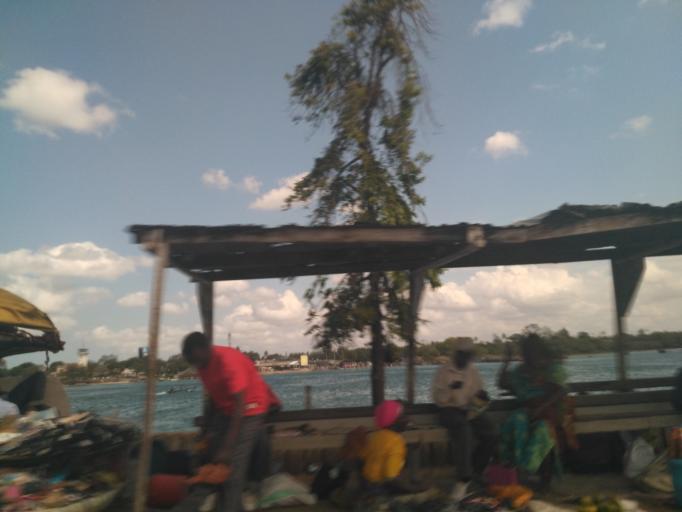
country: TZ
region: Dar es Salaam
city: Dar es Salaam
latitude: -6.8196
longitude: 39.2993
